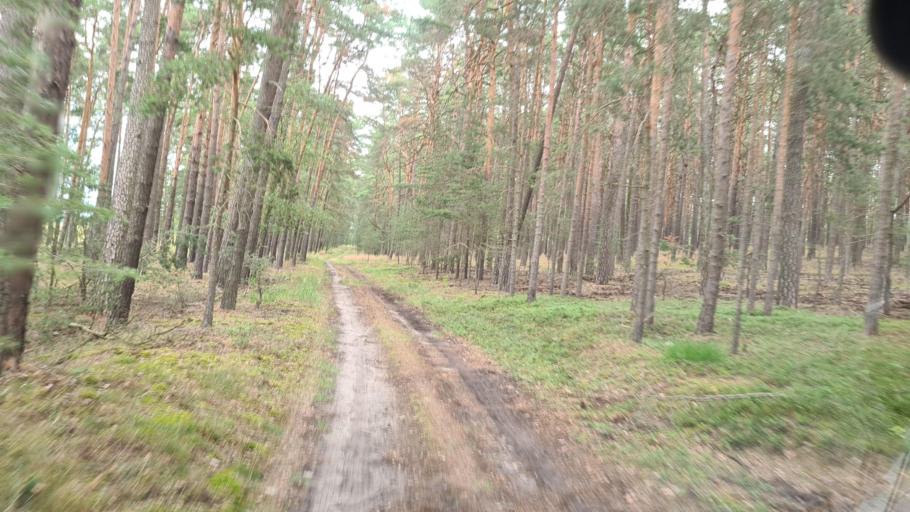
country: DE
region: Brandenburg
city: Crinitz
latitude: 51.7141
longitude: 13.8300
